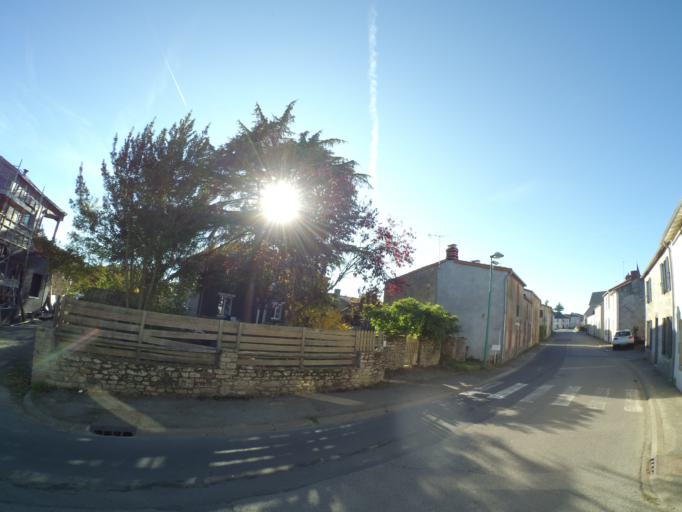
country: FR
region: Pays de la Loire
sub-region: Departement de la Loire-Atlantique
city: Saint-Lumine-de-Clisson
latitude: 47.0827
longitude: -1.3353
